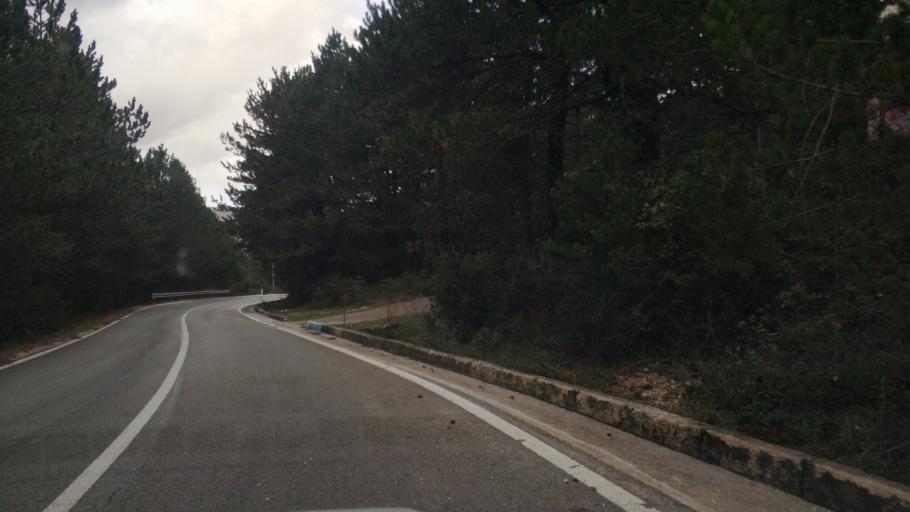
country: AL
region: Vlore
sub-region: Rrethi i Vlores
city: Brataj
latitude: 40.2244
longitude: 19.5786
